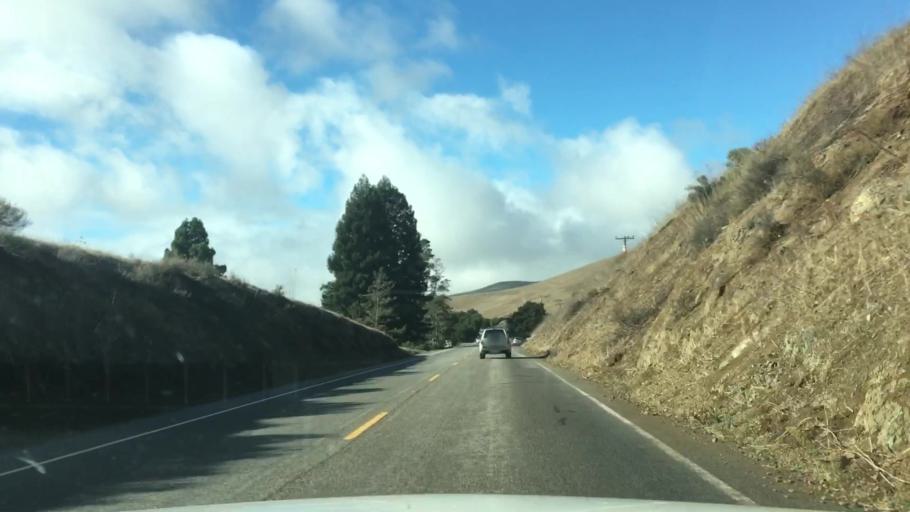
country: US
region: California
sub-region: San Luis Obispo County
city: Morro Bay
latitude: 35.4123
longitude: -120.8046
